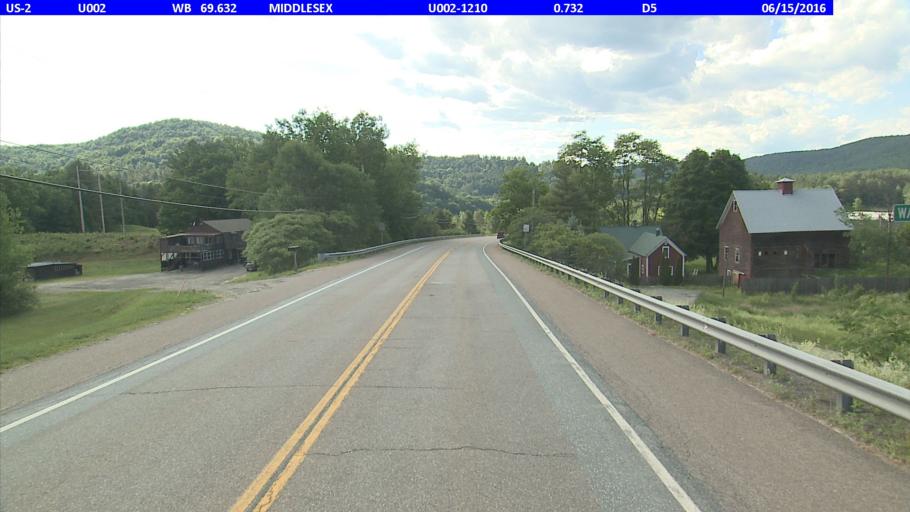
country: US
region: Vermont
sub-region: Washington County
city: Waterbury
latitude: 44.2980
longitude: -72.6882
